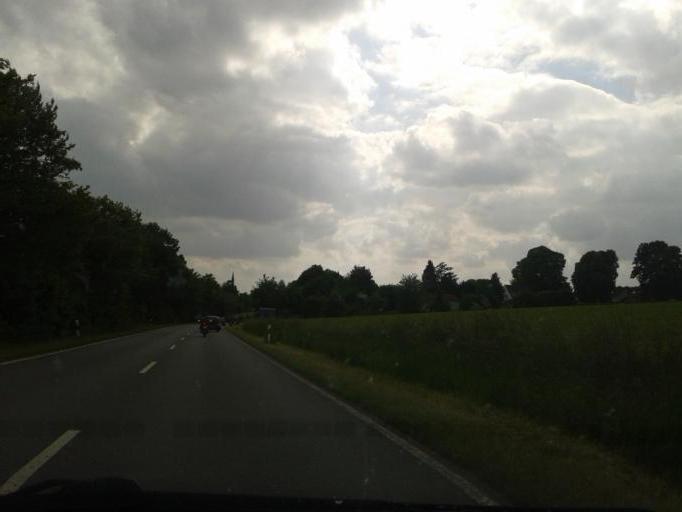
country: DE
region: North Rhine-Westphalia
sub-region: Regierungsbezirk Detmold
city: Steinheim
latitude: 51.9008
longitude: 9.1077
